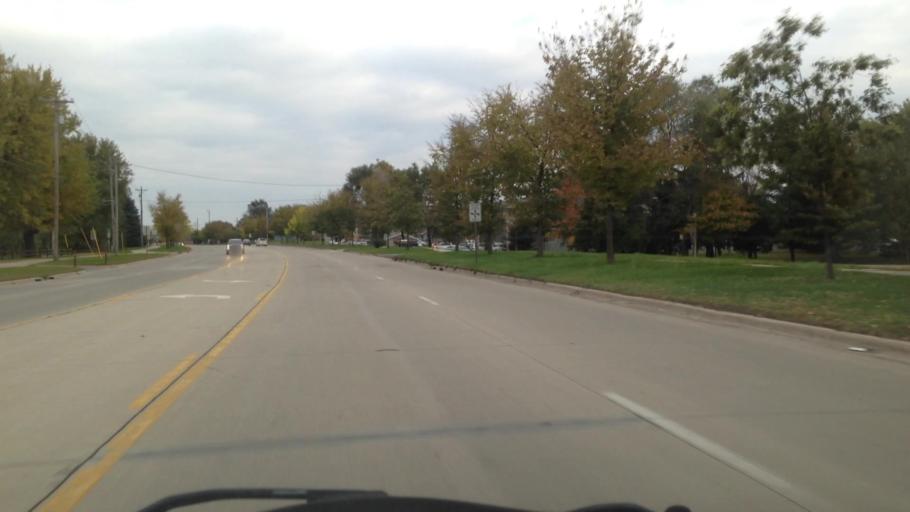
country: US
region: Minnesota
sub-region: Olmsted County
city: Rochester
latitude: 44.0038
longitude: -92.4385
